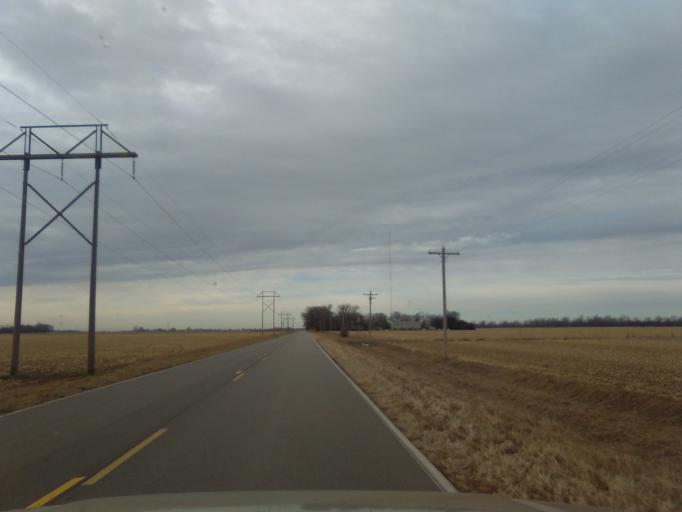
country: US
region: Nebraska
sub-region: Buffalo County
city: Gibbon
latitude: 40.6550
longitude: -98.8416
